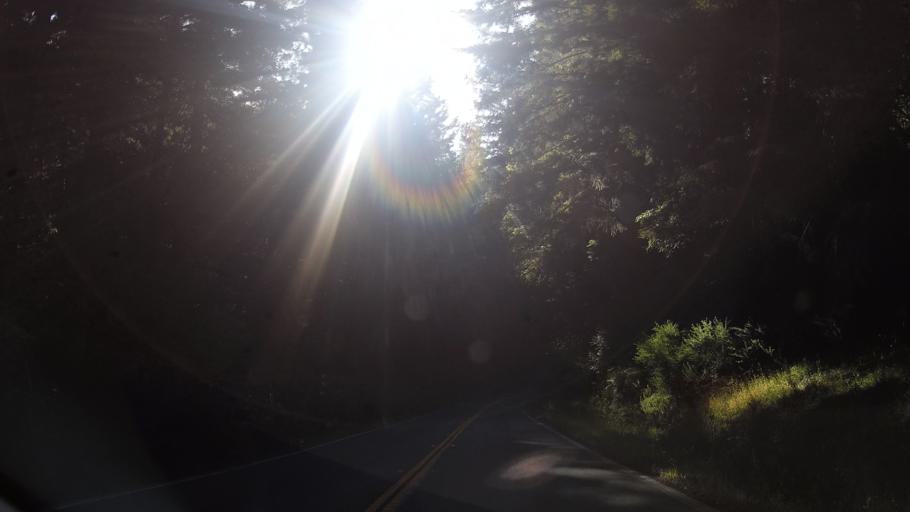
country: US
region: California
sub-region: Mendocino County
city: Brooktrails
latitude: 39.3466
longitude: -123.5654
